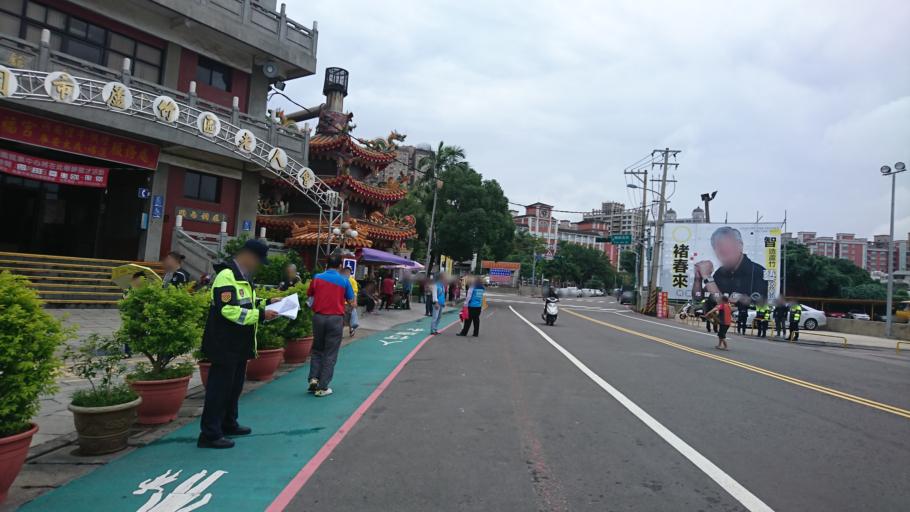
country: TW
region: Taiwan
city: Taoyuan City
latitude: 25.0536
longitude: 121.2951
